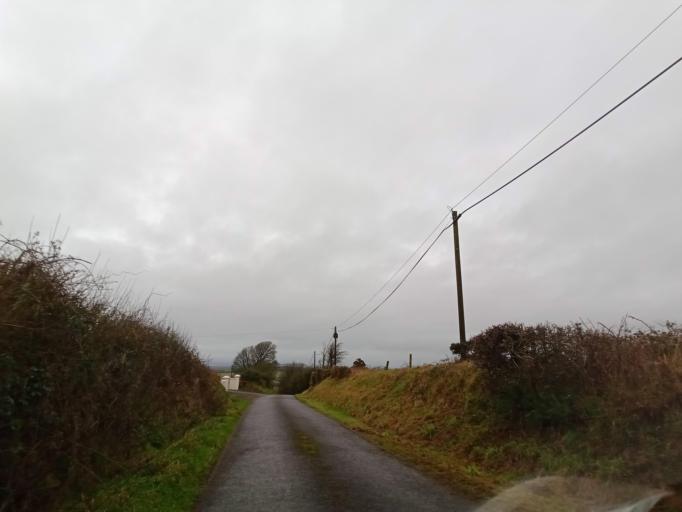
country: IE
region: Munster
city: Fethard
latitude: 52.5571
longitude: -7.7040
